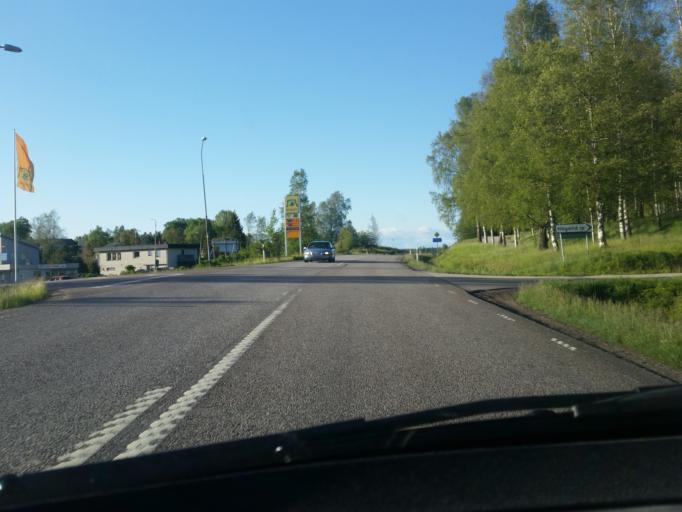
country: SE
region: Vaestra Goetaland
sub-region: Fargelanda Kommun
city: Faergelanda
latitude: 58.5614
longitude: 11.9965
